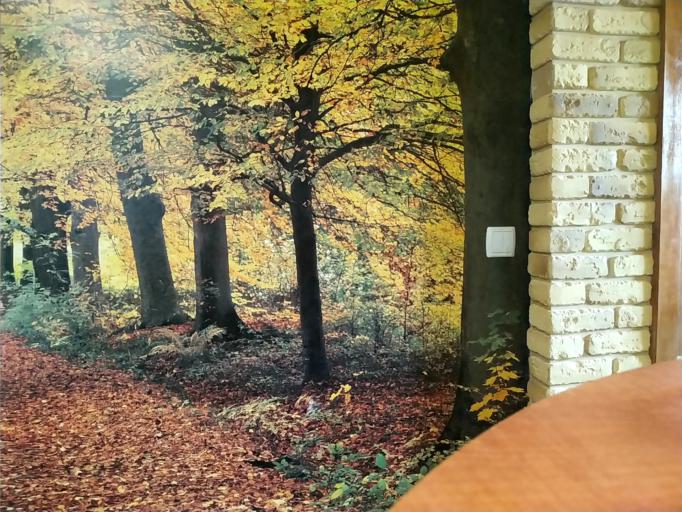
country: RU
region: Novgorod
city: Opechenskiy Posad
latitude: 58.2665
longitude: 34.0296
